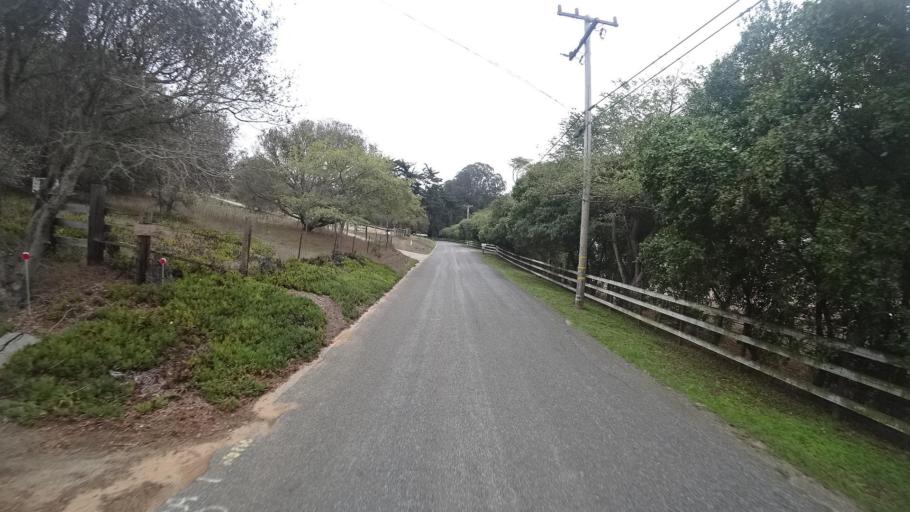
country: US
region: California
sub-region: Monterey County
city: Elkhorn
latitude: 36.8253
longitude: -121.7029
